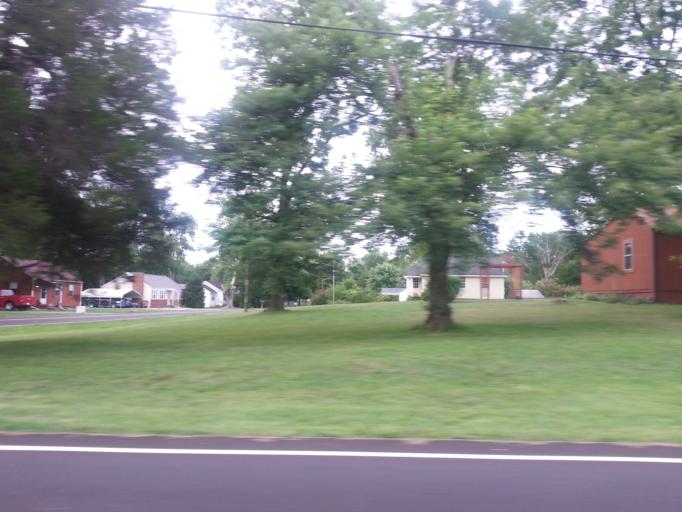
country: US
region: Tennessee
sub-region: Knox County
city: Knoxville
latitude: 36.0167
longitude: -83.9018
